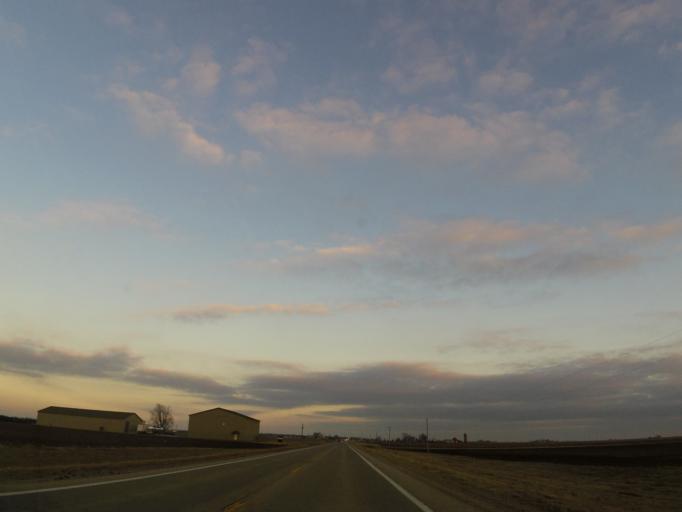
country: US
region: Illinois
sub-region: McLean County
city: Gridley
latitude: 40.7391
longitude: -88.9221
